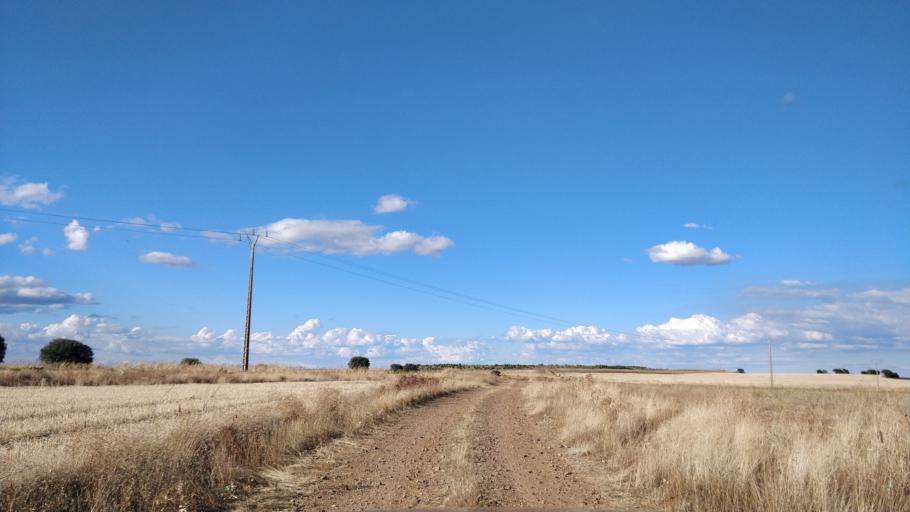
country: ES
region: Castille and Leon
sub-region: Provincia de Leon
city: Santa Cristina de Valmadrigal
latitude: 42.3396
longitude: -5.2732
